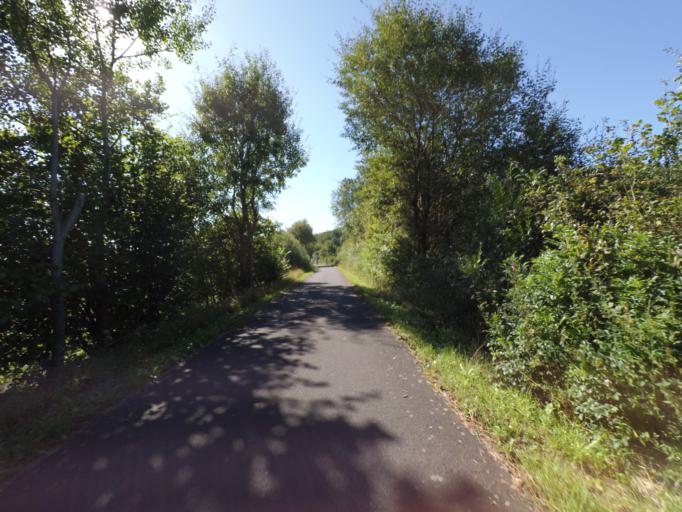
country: DE
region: Rheinland-Pfalz
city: Udler
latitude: 50.1322
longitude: 6.8900
